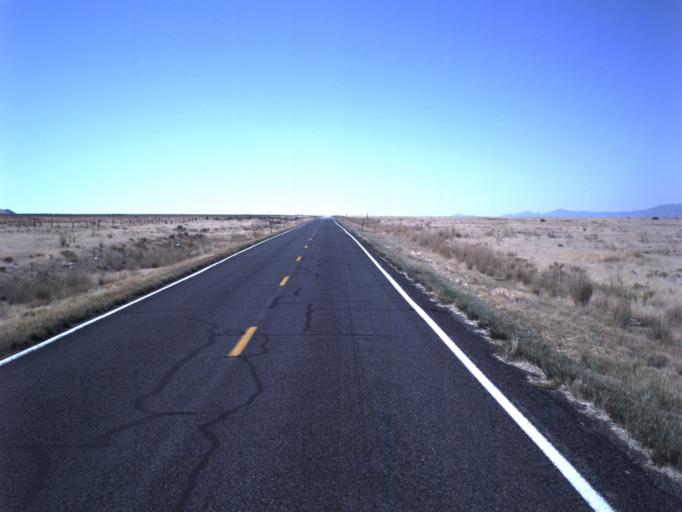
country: US
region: Utah
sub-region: Tooele County
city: Grantsville
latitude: 40.6040
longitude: -112.7109
